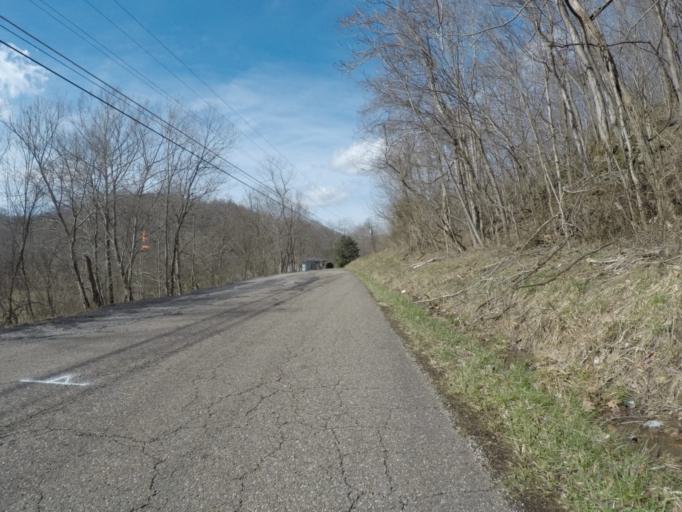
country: US
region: Ohio
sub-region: Lawrence County
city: Burlington
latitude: 38.4780
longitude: -82.5026
